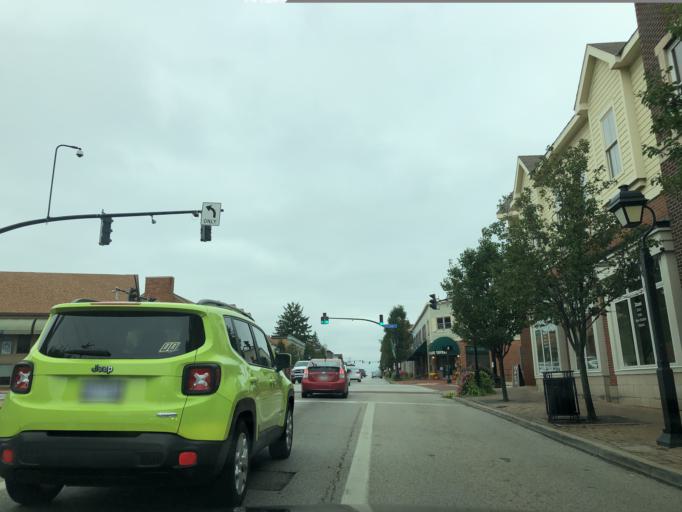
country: US
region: Ohio
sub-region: Hamilton County
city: Montgomery
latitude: 39.2261
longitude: -84.3550
